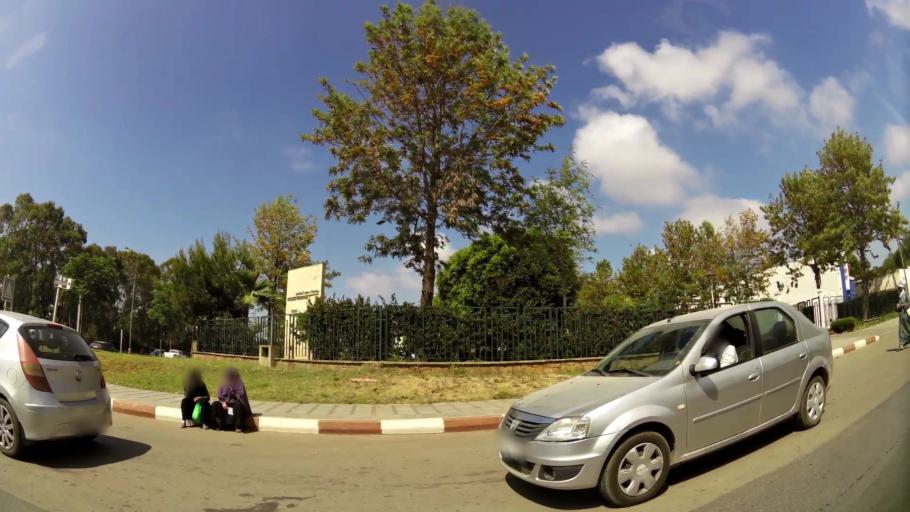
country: MA
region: Rabat-Sale-Zemmour-Zaer
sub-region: Rabat
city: Rabat
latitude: 33.9872
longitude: -6.8594
